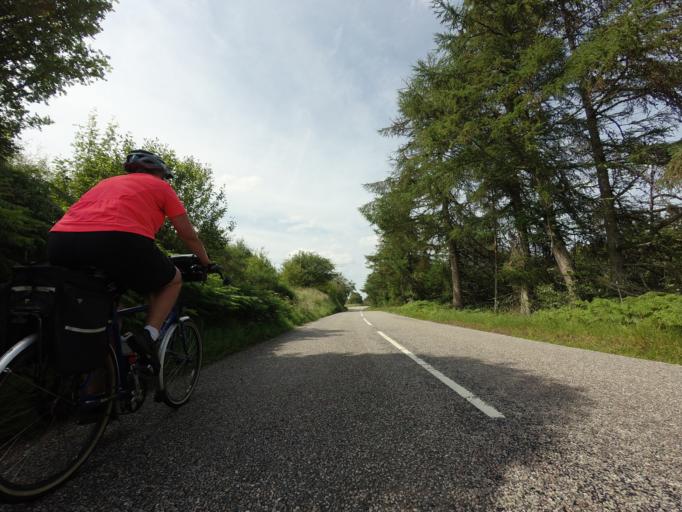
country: GB
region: Scotland
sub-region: Highland
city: Alness
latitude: 57.8564
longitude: -4.2275
